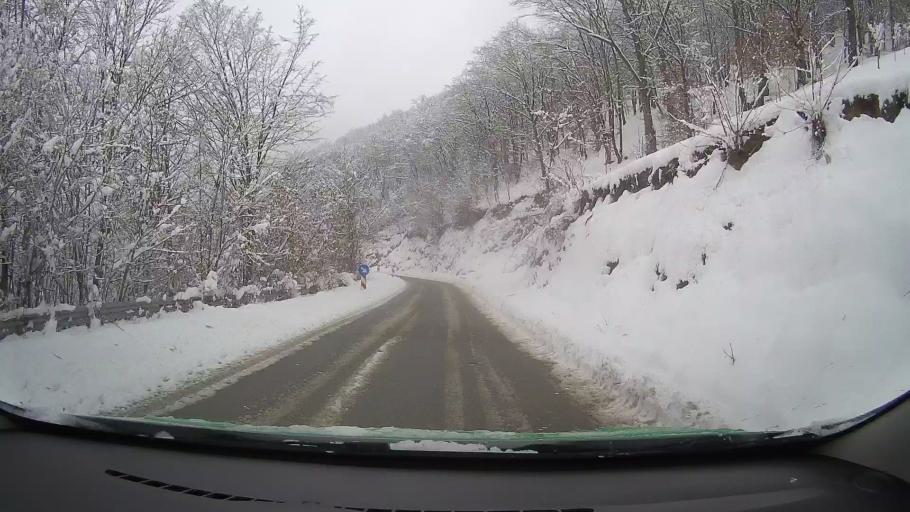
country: RO
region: Alba
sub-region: Comuna Sugag
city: Dobra
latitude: 45.7579
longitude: 23.6640
